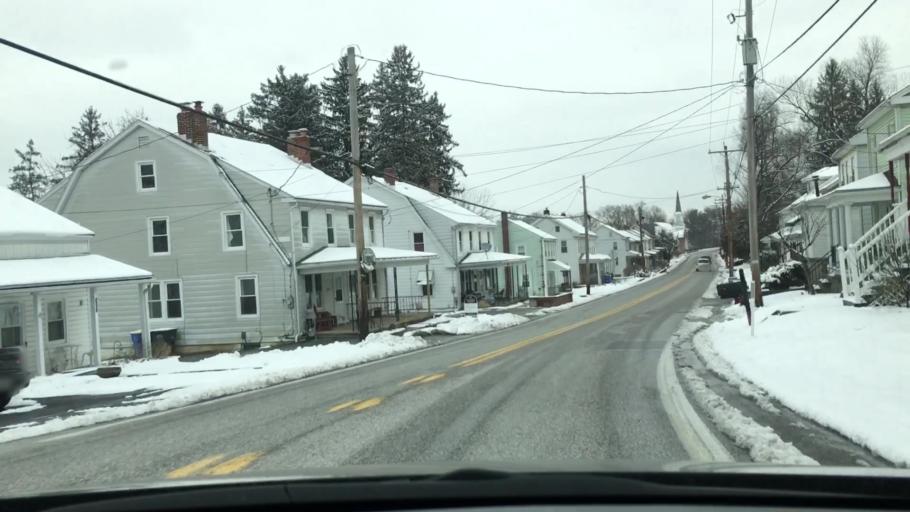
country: US
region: Pennsylvania
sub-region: York County
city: Emigsville
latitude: 40.0015
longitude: -76.7056
